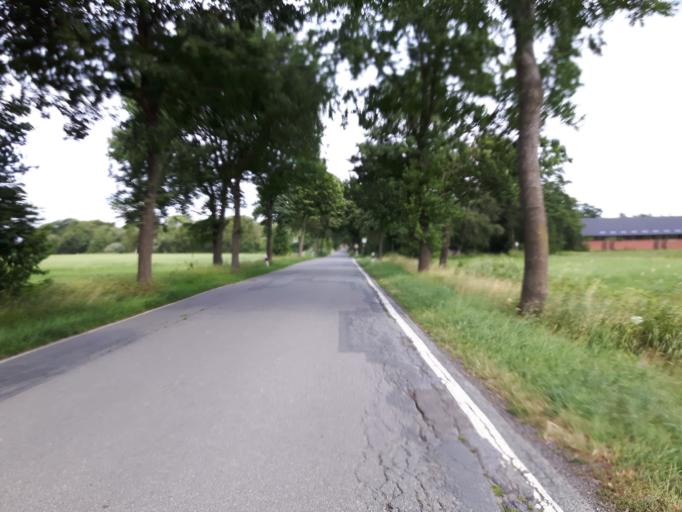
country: DE
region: Lower Saxony
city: Ovelgonne
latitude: 53.2700
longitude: 8.3347
